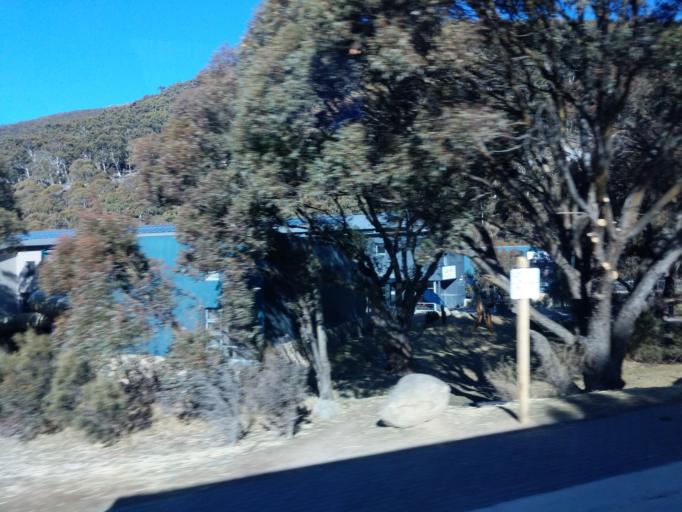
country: AU
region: New South Wales
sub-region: Snowy River
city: Jindabyne
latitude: -36.5010
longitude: 148.3101
